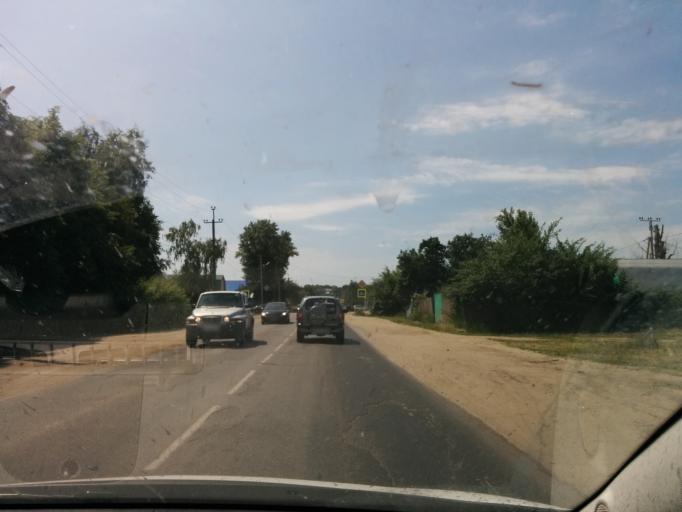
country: RU
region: Tambov
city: Morshansk
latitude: 53.4466
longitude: 41.8074
